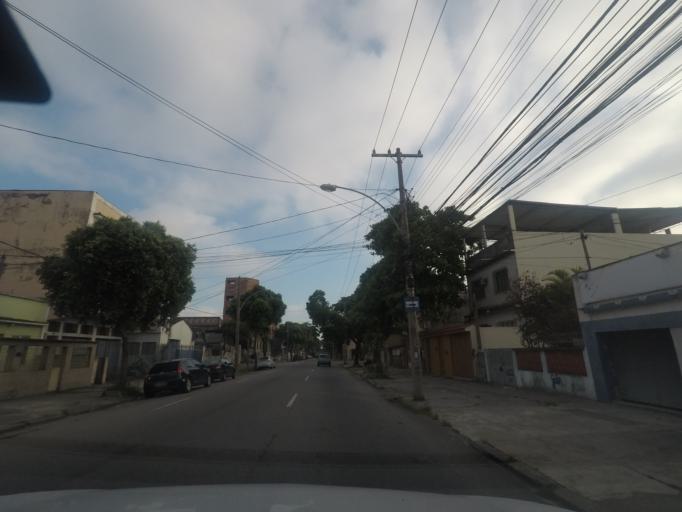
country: BR
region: Rio de Janeiro
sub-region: Duque De Caxias
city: Duque de Caxias
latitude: -22.8349
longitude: -43.2778
